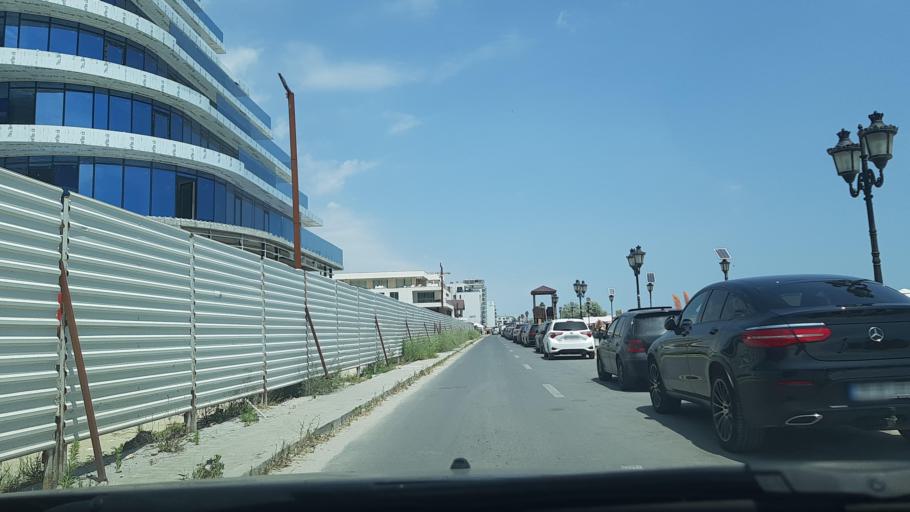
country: RO
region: Constanta
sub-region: Comuna Navodari
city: Navodari
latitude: 44.2893
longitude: 28.6230
